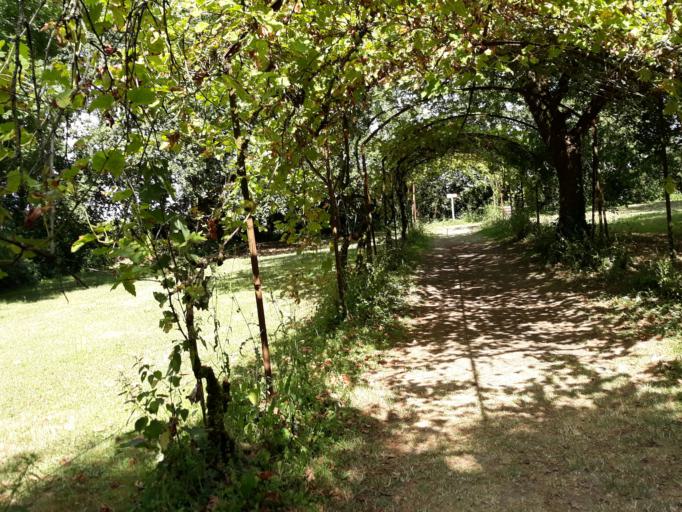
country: FR
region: Poitou-Charentes
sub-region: Departement de la Charente-Maritime
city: Pons
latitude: 45.5684
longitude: -0.5359
